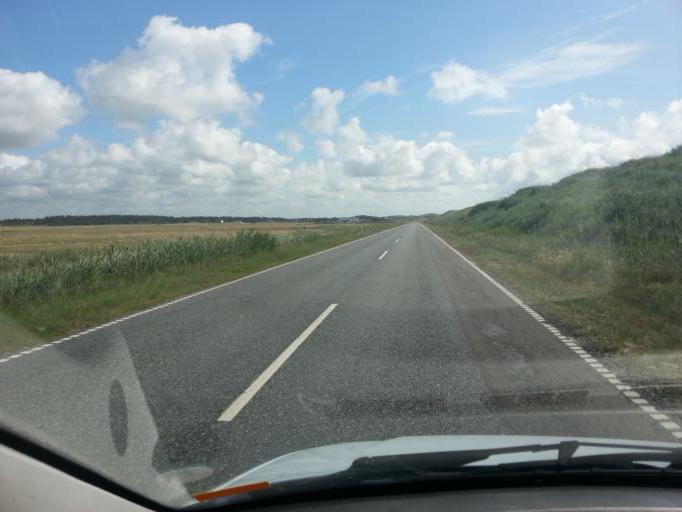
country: DK
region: Central Jutland
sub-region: Holstebro Kommune
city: Ulfborg
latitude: 56.3302
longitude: 8.1231
